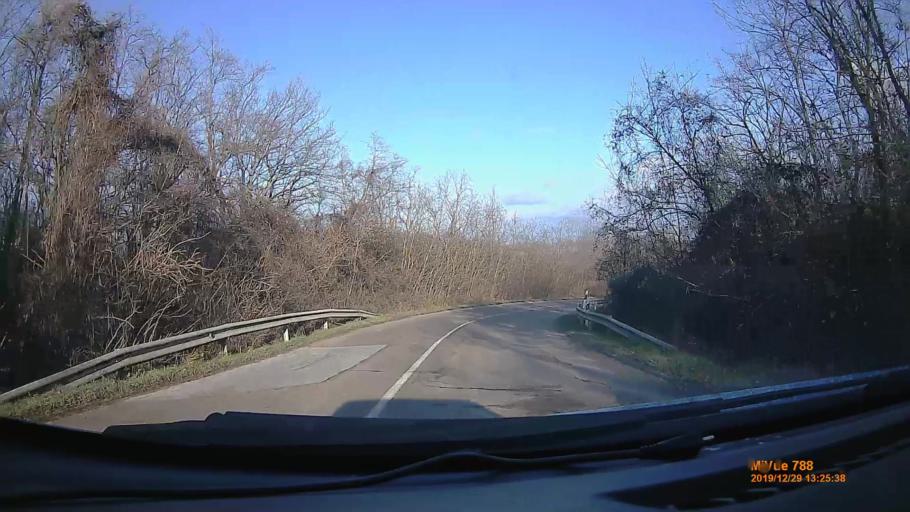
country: HU
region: Heves
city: Verpelet
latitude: 47.8491
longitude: 20.1977
